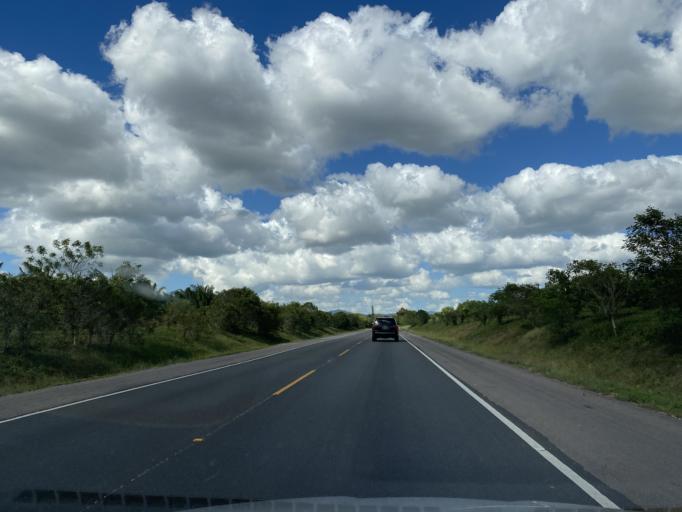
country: DO
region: Monte Plata
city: Monte Plata
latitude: 18.7380
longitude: -69.7631
